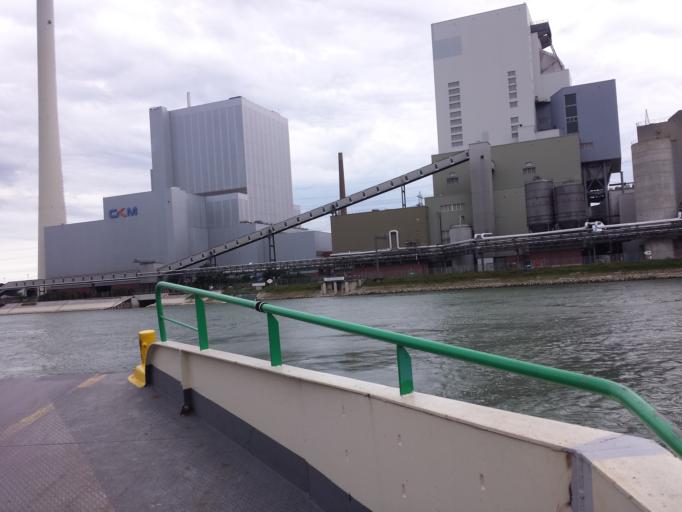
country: DE
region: Rheinland-Pfalz
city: Altrip
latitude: 49.4413
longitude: 8.5006
